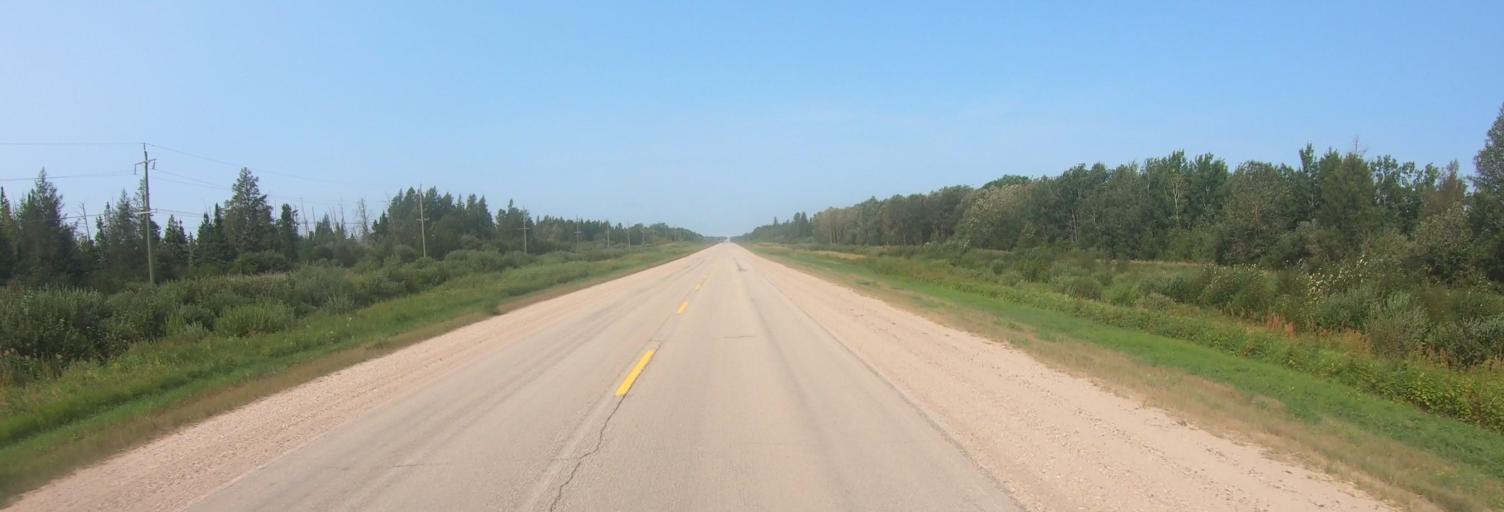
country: US
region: Minnesota
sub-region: Roseau County
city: Roseau
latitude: 49.0896
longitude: -95.9141
